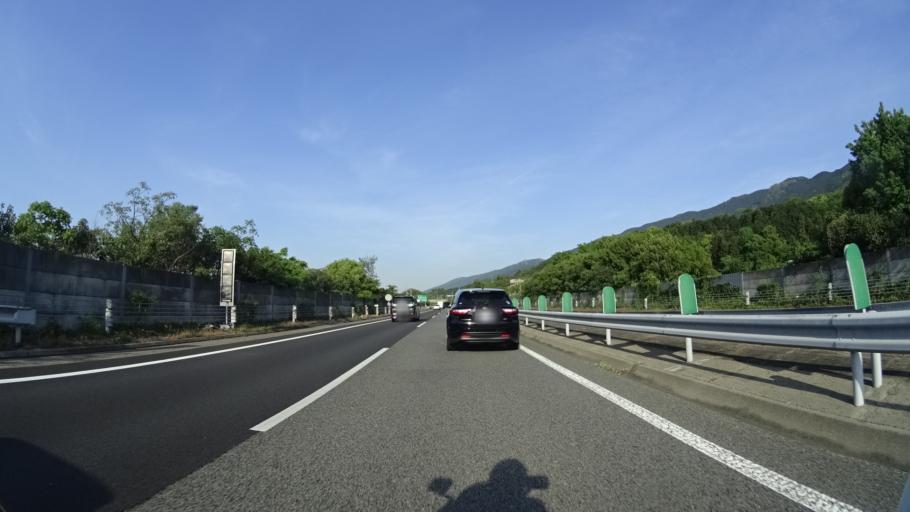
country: JP
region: Ehime
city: Kawanoecho
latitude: 33.9762
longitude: 133.5651
